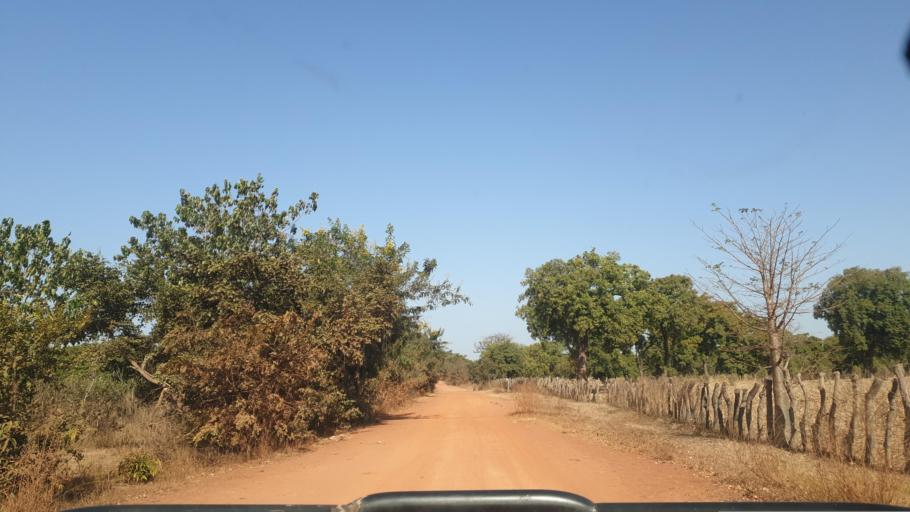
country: ML
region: Sikasso
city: Bougouni
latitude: 11.7730
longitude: -6.9034
